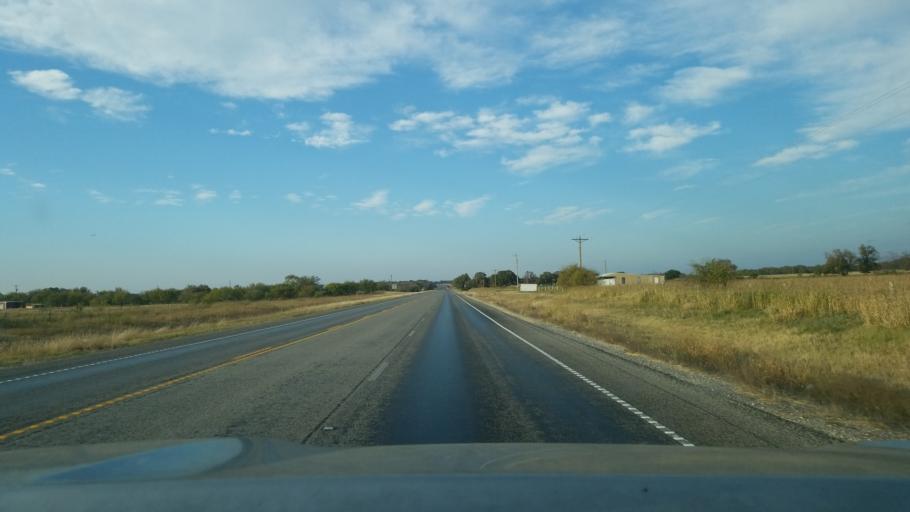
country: US
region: Texas
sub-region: Brown County
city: Lake Brownwood
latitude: 31.9951
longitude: -98.9209
